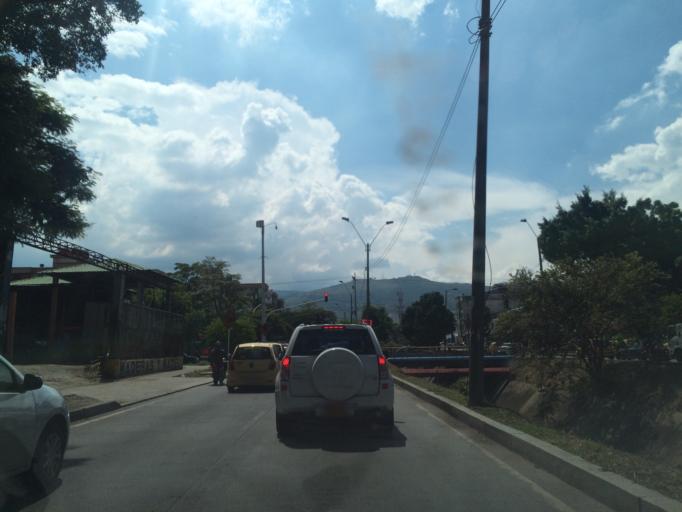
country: CO
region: Valle del Cauca
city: Cali
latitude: 3.4191
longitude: -76.5305
